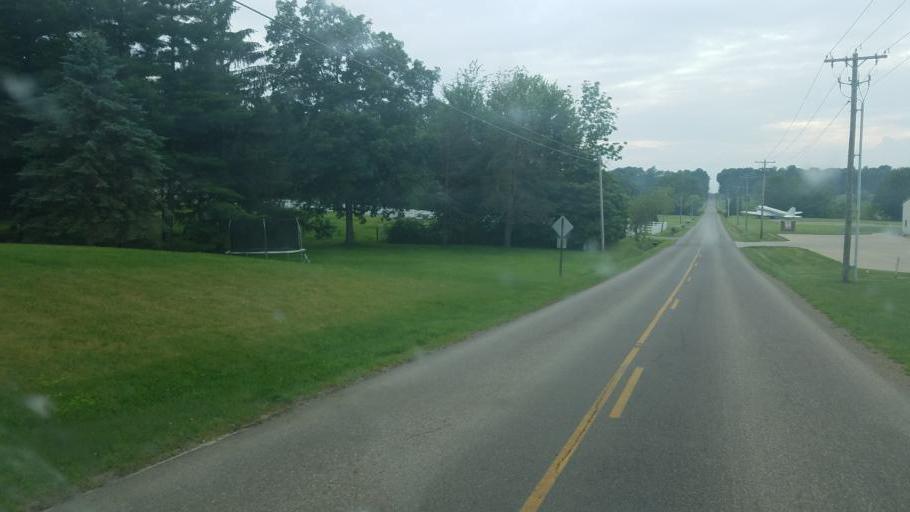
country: US
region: Ohio
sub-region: Wayne County
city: Apple Creek
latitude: 40.7559
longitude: -81.7765
